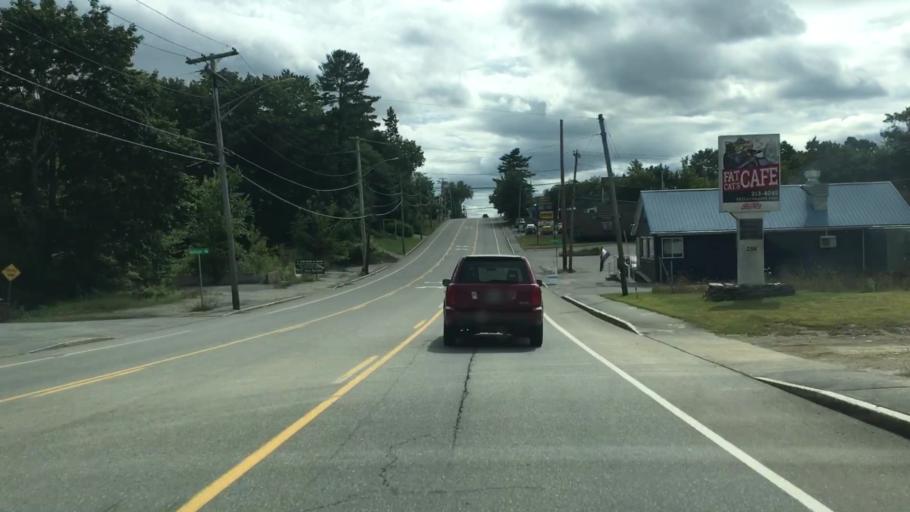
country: US
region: Maine
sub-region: Kennebec County
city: Augusta
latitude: 44.3033
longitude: -69.7819
